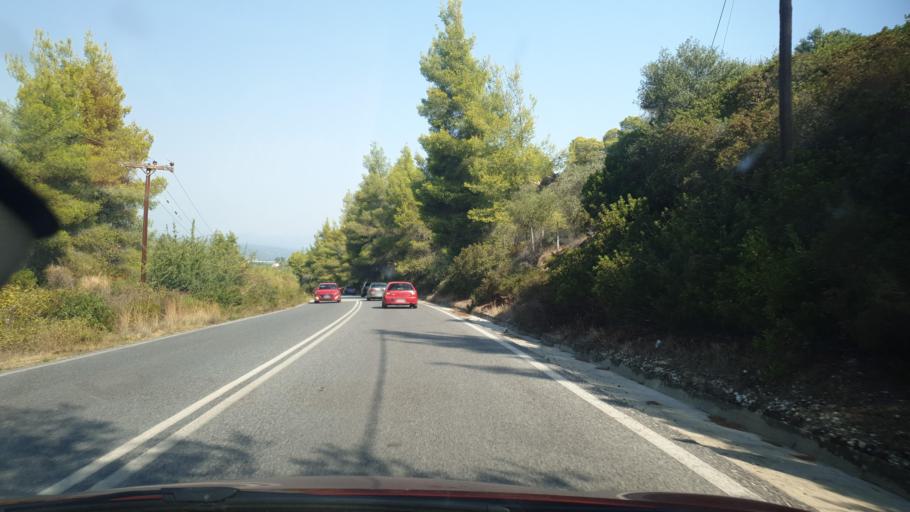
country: GR
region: Central Macedonia
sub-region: Nomos Chalkidikis
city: Agios Nikolaos
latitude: 40.2125
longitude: 23.7562
